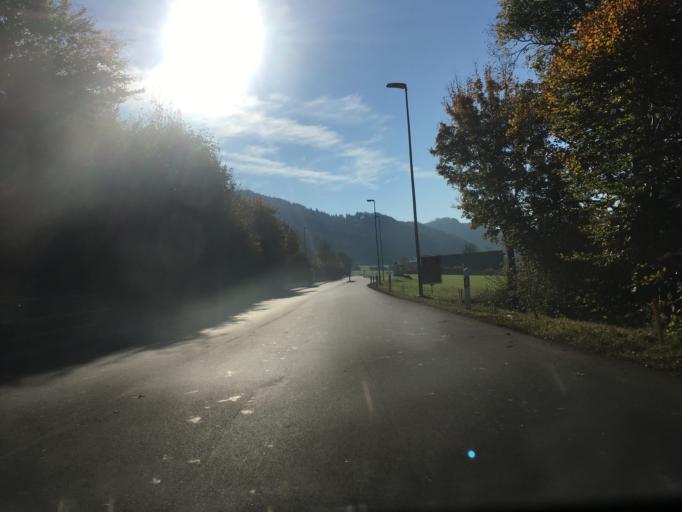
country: CH
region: Zurich
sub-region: Bezirk Affoltern
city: Sellenbueren
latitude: 47.3396
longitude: 8.4845
